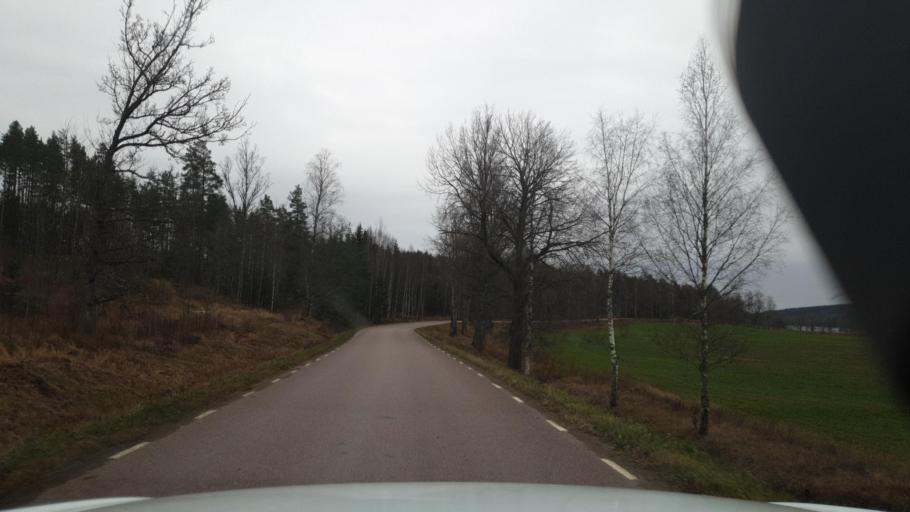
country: SE
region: Vaermland
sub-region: Karlstads Kommun
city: Valberg
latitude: 59.4423
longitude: 13.0902
